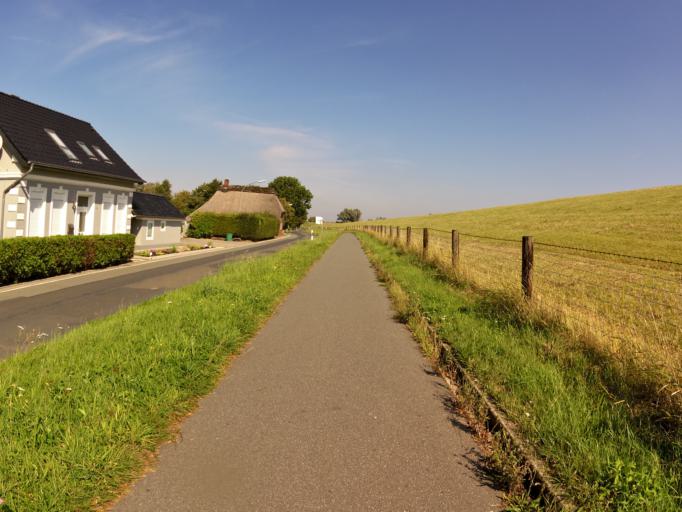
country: DE
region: Lower Saxony
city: Elsfleth
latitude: 53.2801
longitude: 8.4814
